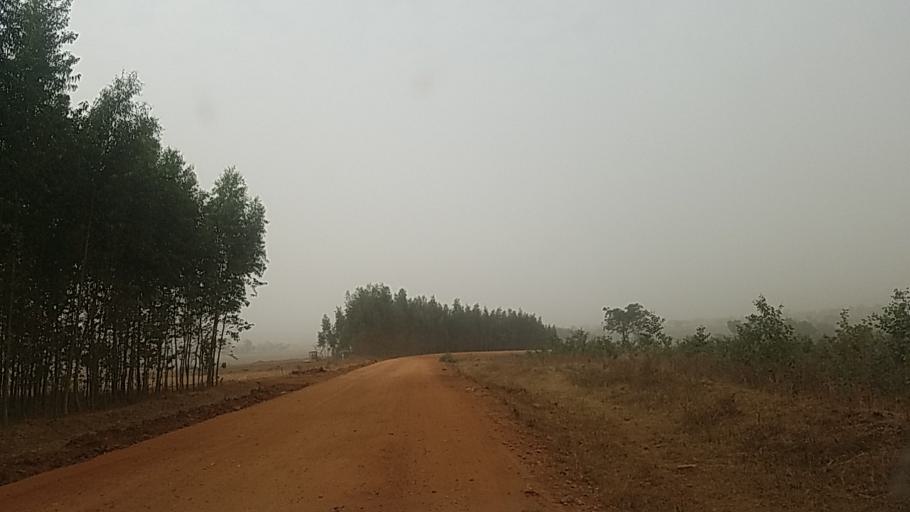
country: ET
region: Amhara
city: Bure
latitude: 10.8606
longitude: 36.4011
